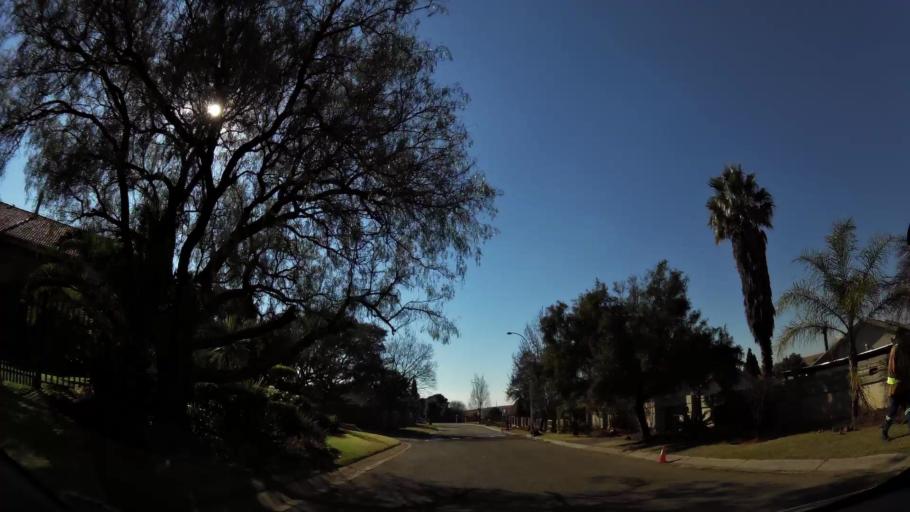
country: ZA
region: Mpumalanga
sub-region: Nkangala District Municipality
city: Witbank
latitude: -25.8759
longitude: 29.2517
